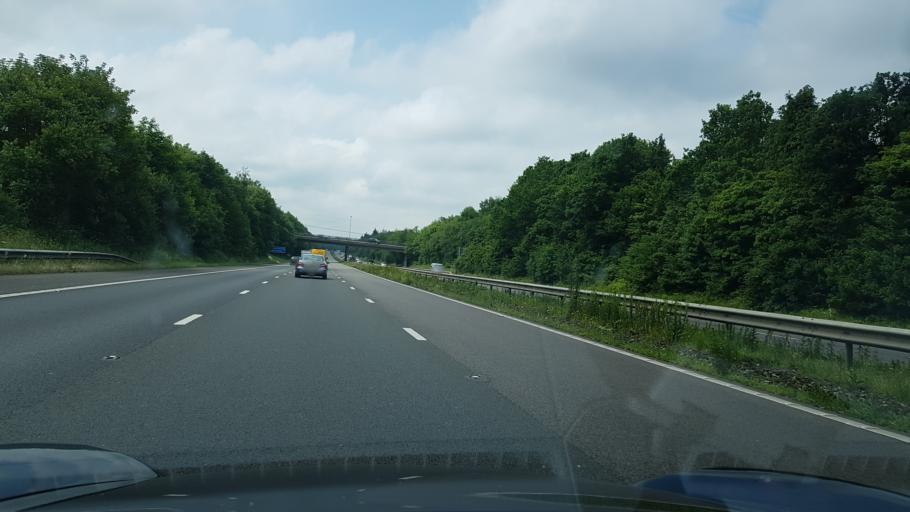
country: GB
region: England
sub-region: West Sussex
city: Maidenbower
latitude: 51.1054
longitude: -0.1428
